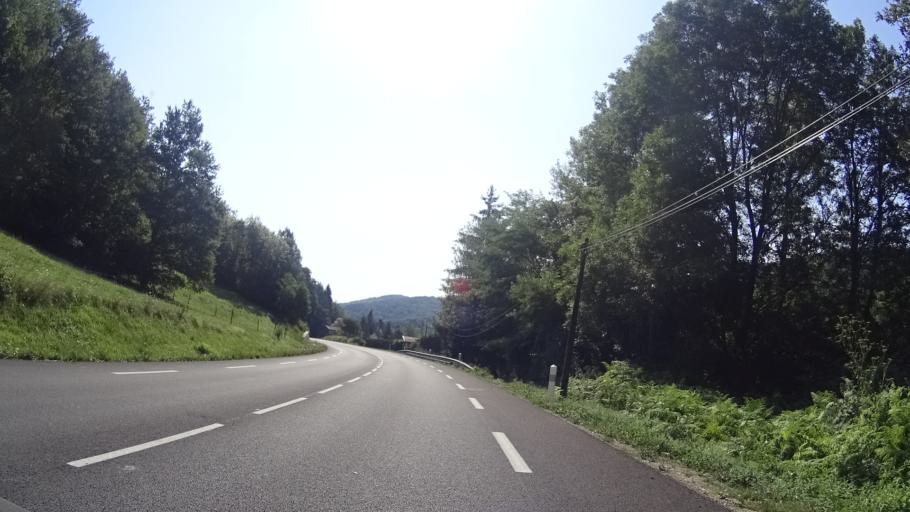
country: FR
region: Midi-Pyrenees
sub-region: Departement de l'Ariege
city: Lavelanet
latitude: 42.9141
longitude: 1.7715
